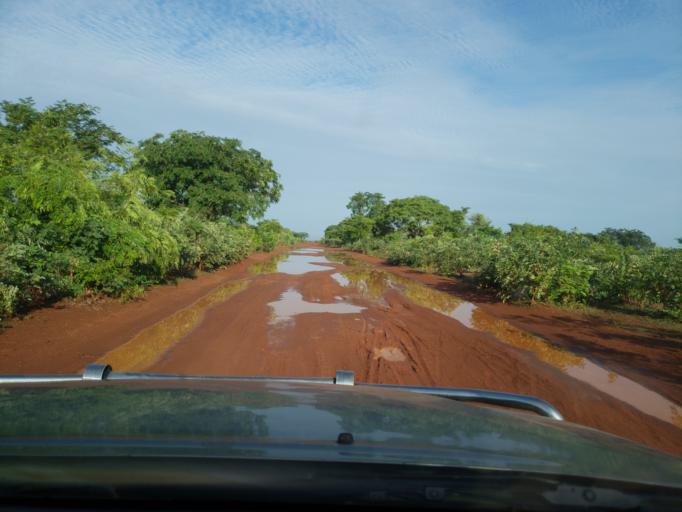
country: ML
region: Sikasso
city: Koutiala
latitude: 12.4270
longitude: -5.6367
